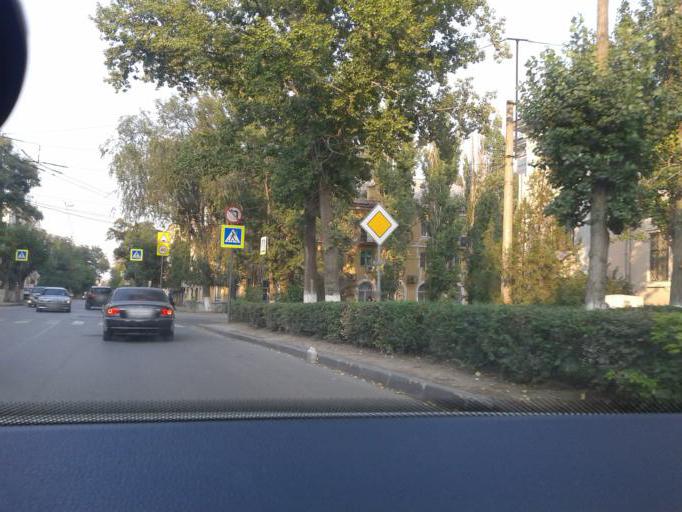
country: RU
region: Volgograd
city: Volgograd
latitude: 48.6964
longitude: 44.5034
